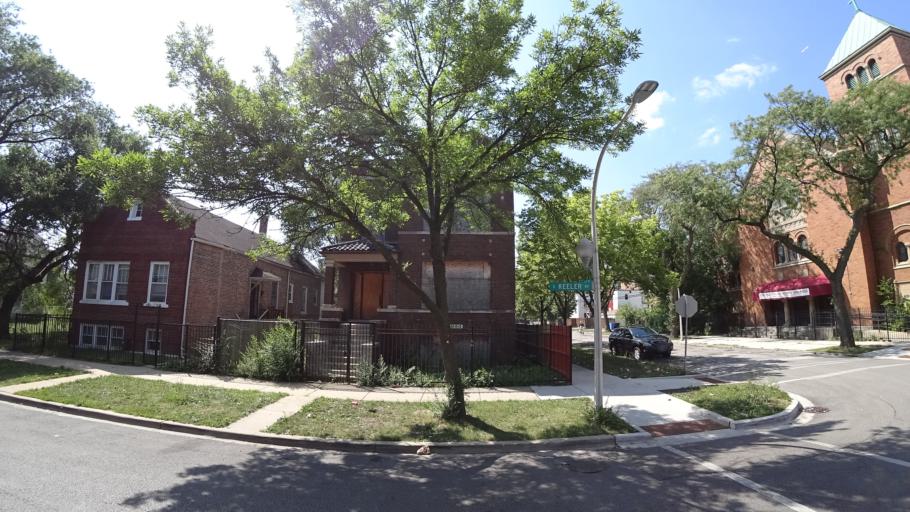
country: US
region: Illinois
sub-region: Cook County
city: Cicero
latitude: 41.8605
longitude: -87.7299
